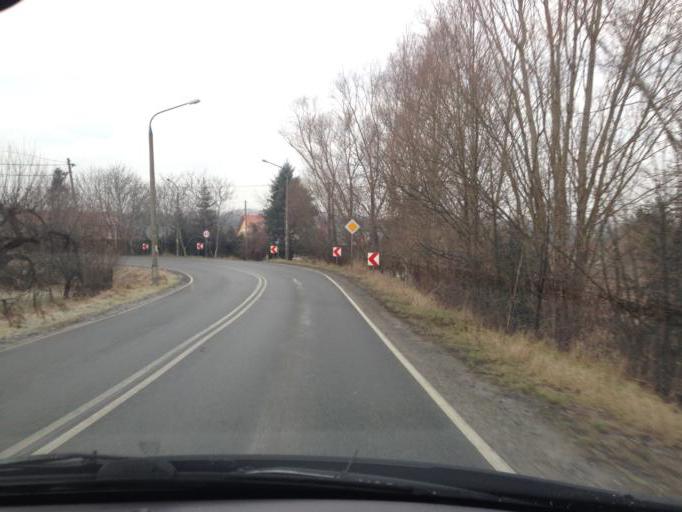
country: PL
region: Lesser Poland Voivodeship
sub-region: Powiat wielicki
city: Kokotow
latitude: 50.0569
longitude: 20.0681
